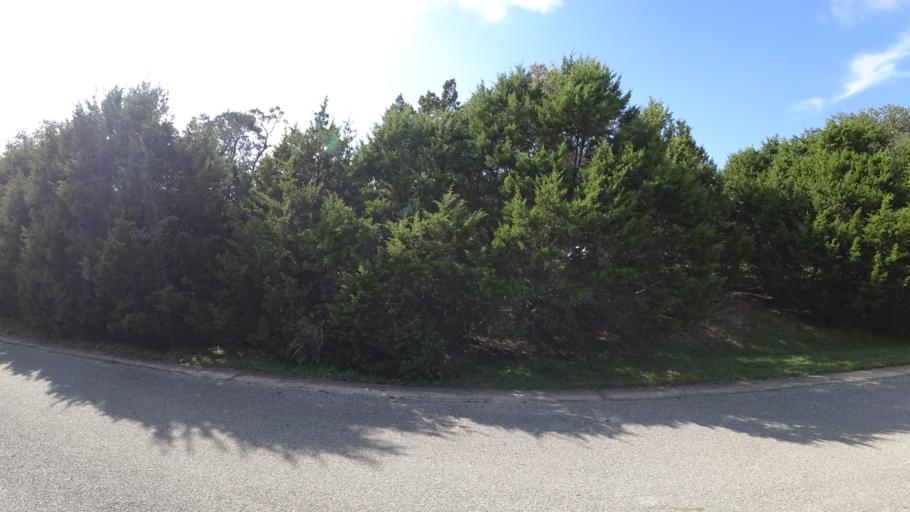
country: US
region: Texas
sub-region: Travis County
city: Lost Creek
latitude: 30.3026
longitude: -97.8507
